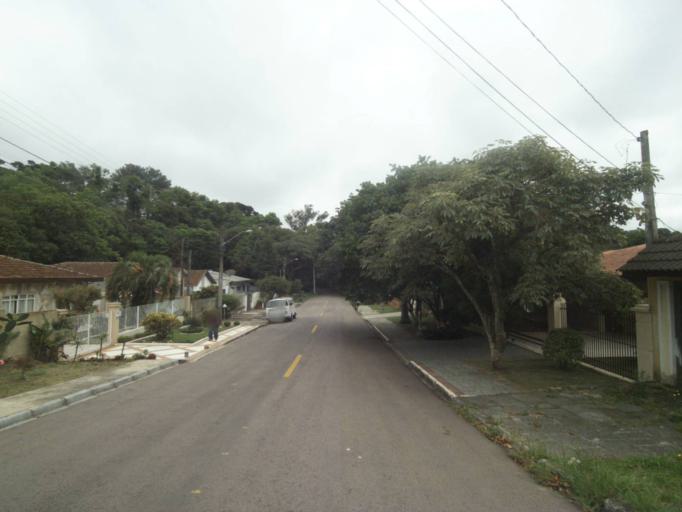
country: BR
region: Parana
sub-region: Curitiba
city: Curitiba
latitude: -25.3990
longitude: -49.2762
